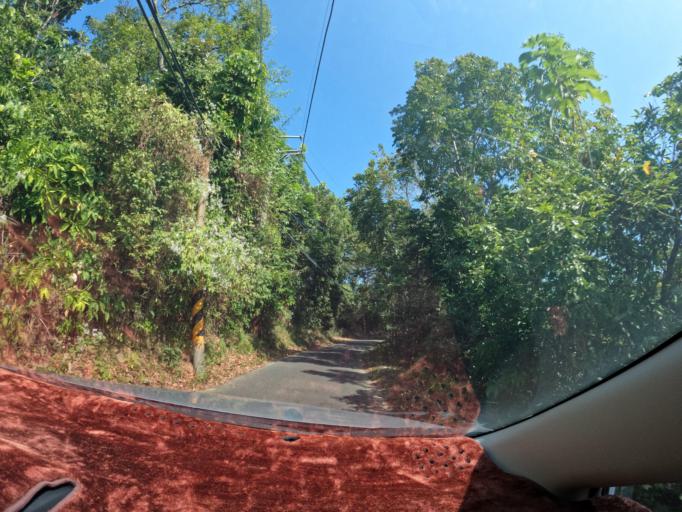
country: TW
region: Taiwan
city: Yujing
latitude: 23.0489
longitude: 120.3793
